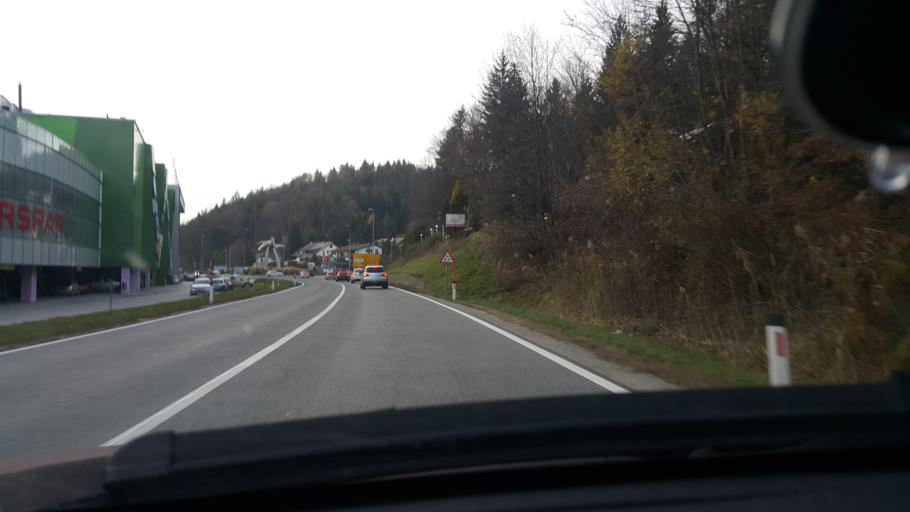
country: SI
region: Velenje
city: Velenje
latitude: 46.3522
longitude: 15.1290
